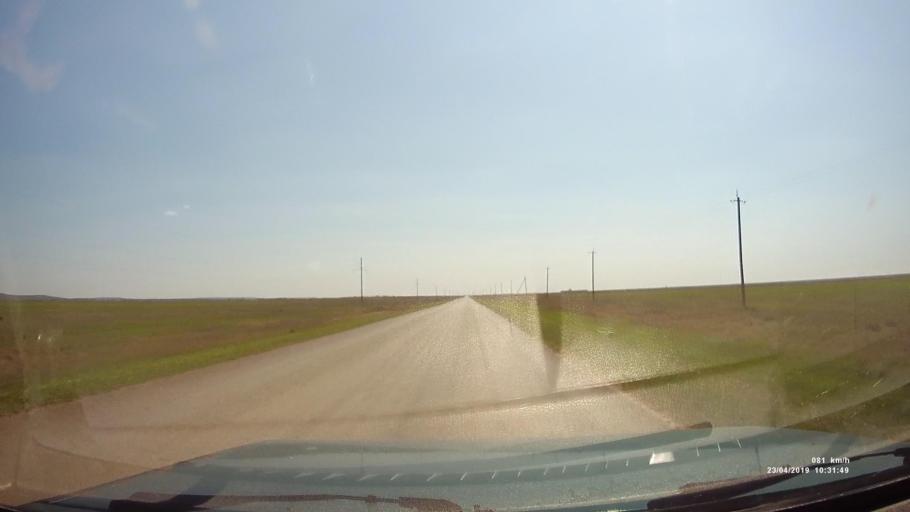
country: RU
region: Kalmykiya
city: Yashalta
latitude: 46.5840
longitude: 42.5674
